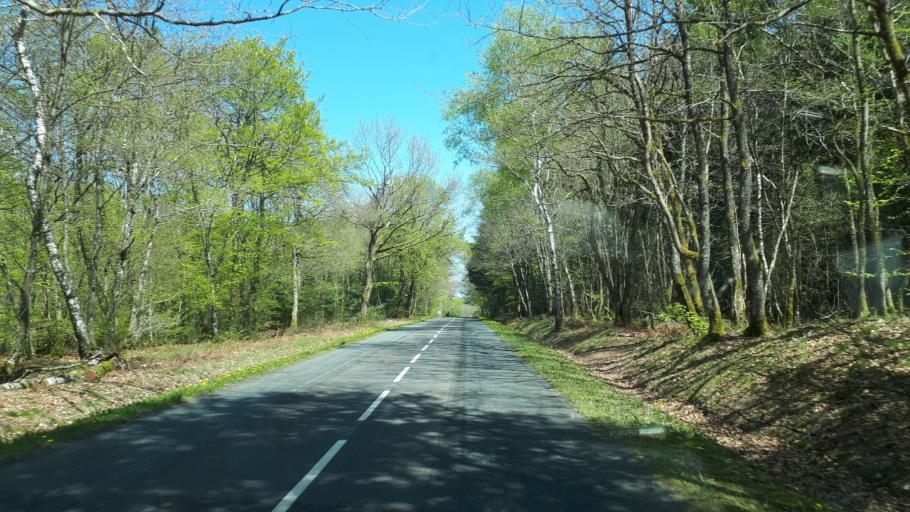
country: FR
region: Centre
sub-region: Departement du Cher
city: Henrichemont
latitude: 47.3011
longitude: 2.6189
